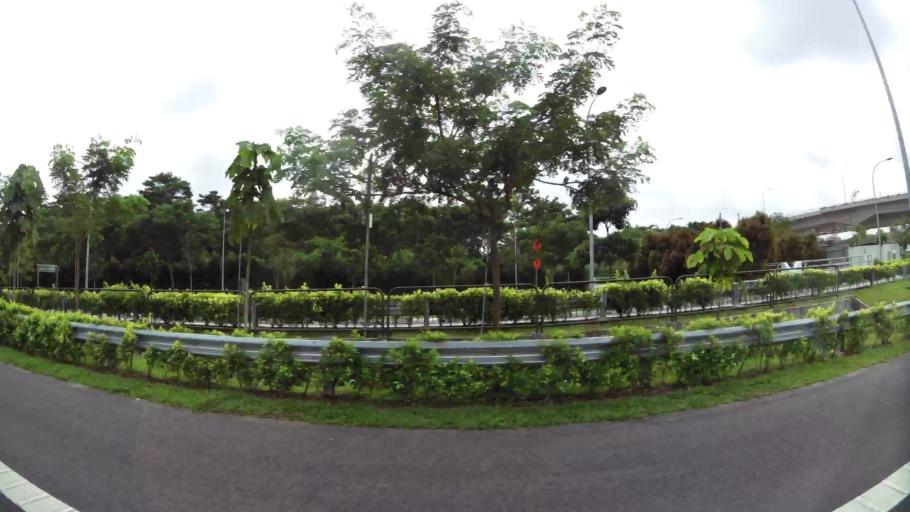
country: MY
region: Johor
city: Kampung Pasir Gudang Baru
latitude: 1.4002
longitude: 103.8580
